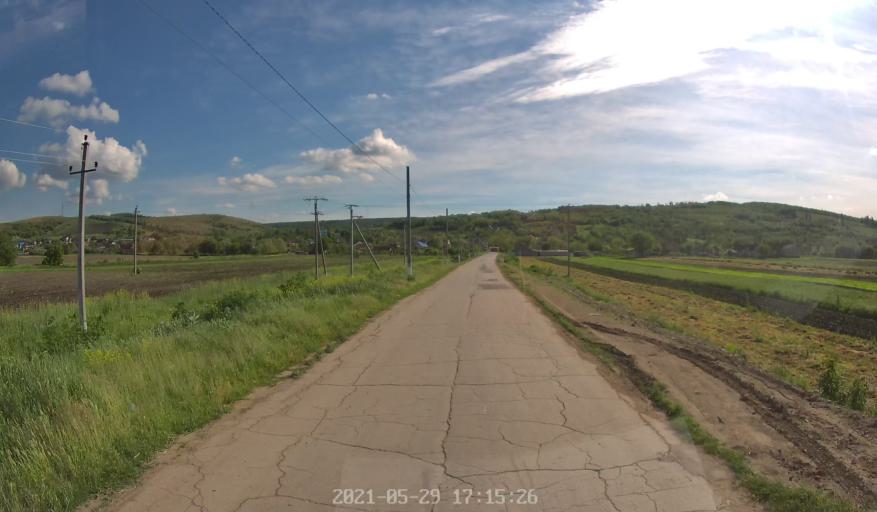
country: MD
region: Laloveni
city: Ialoveni
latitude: 46.8316
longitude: 28.8455
